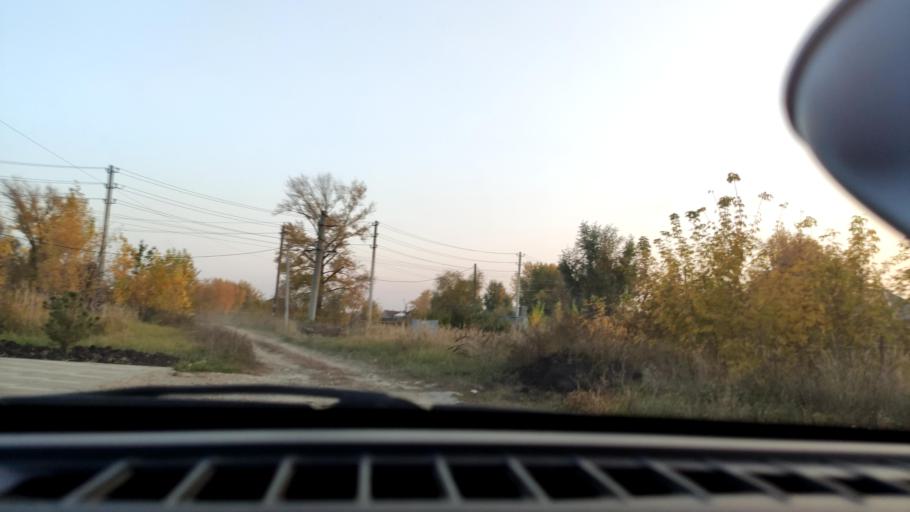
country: RU
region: Samara
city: Samara
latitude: 53.1490
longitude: 50.0862
